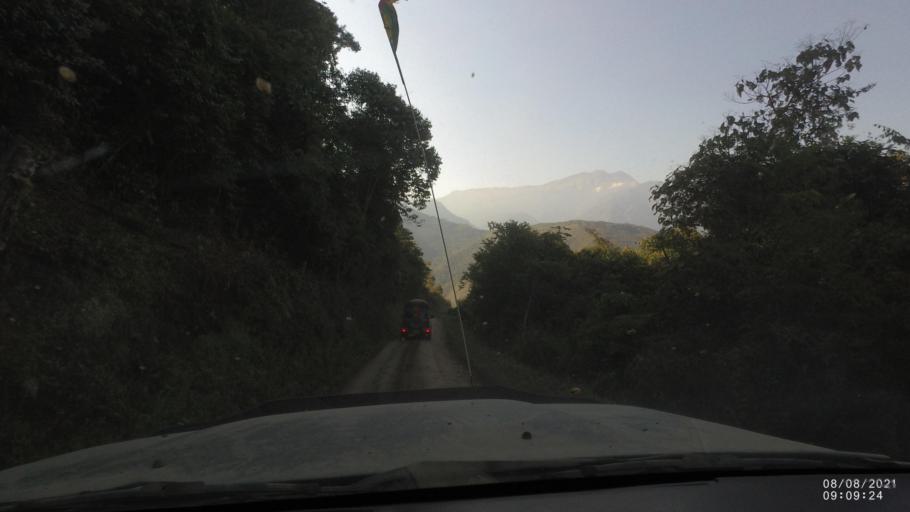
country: BO
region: La Paz
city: Quime
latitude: -16.5688
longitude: -66.7321
